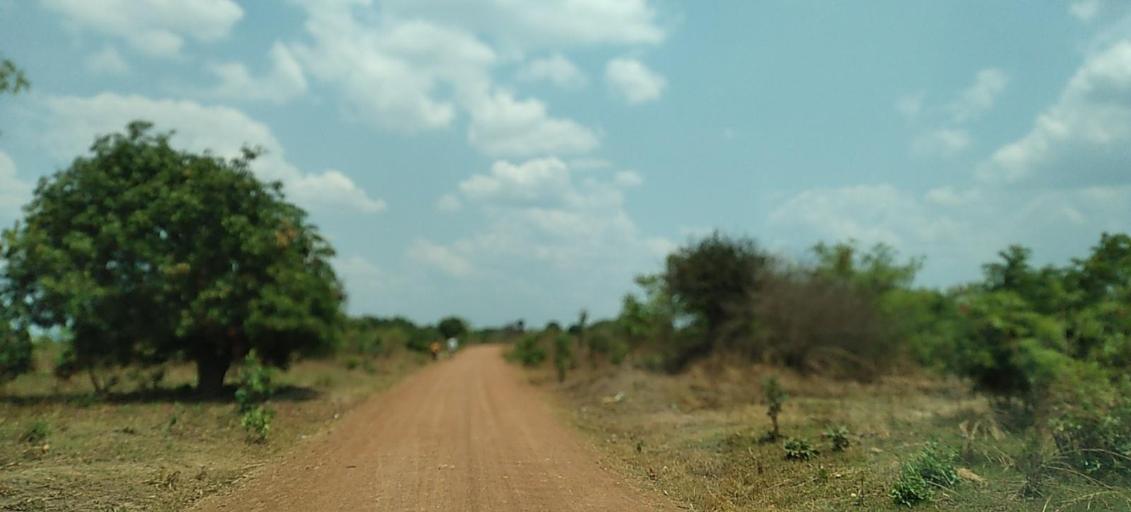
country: ZM
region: Copperbelt
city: Luanshya
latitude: -13.1299
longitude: 28.3125
